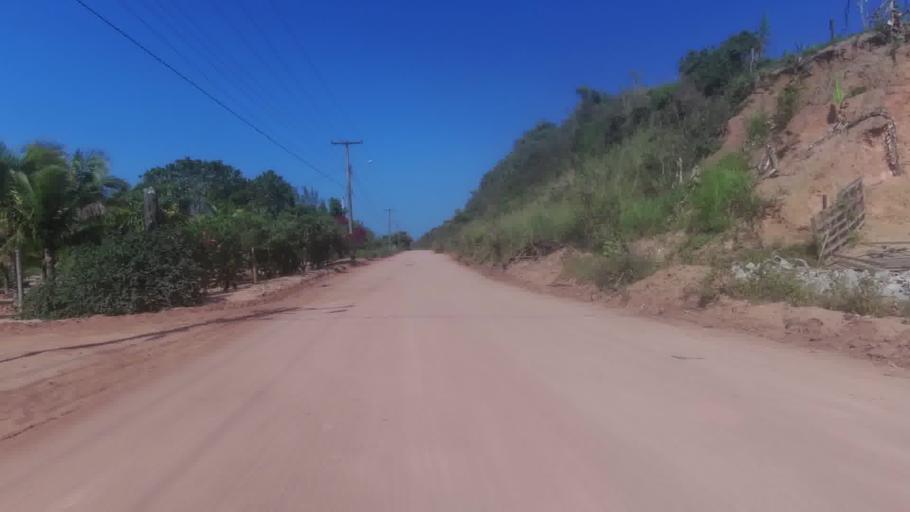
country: BR
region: Espirito Santo
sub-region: Marataizes
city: Marataizes
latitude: -21.0753
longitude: -40.8405
